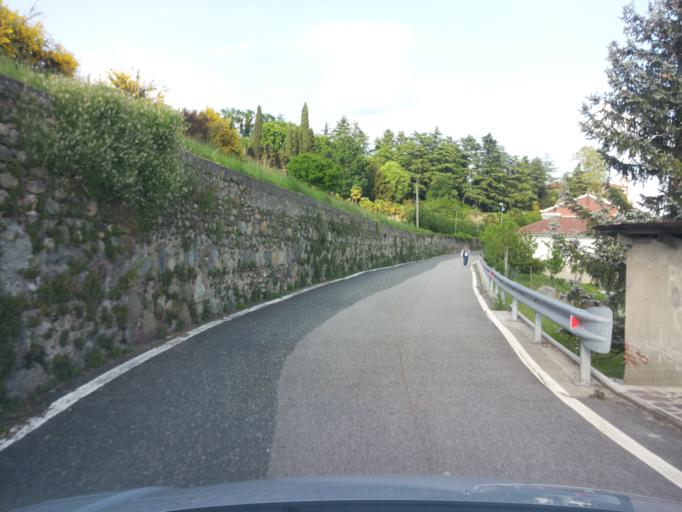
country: IT
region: Piedmont
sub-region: Provincia di Torino
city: Azeglio
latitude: 45.4250
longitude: 7.9892
